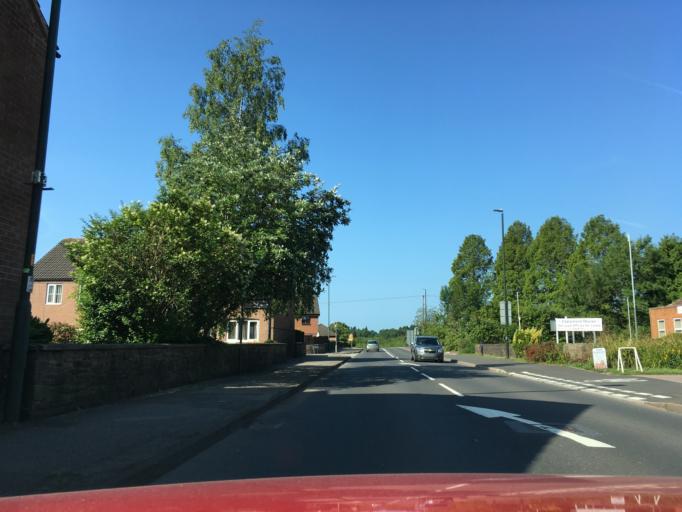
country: GB
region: England
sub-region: Gloucestershire
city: Lydney
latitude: 51.7230
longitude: -2.5386
